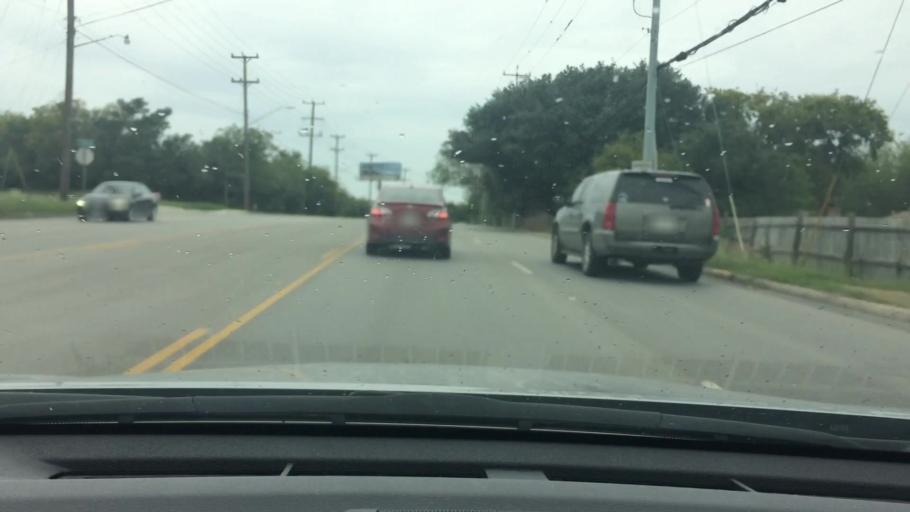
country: US
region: Texas
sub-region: Bexar County
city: Converse
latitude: 29.5370
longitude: -98.3338
